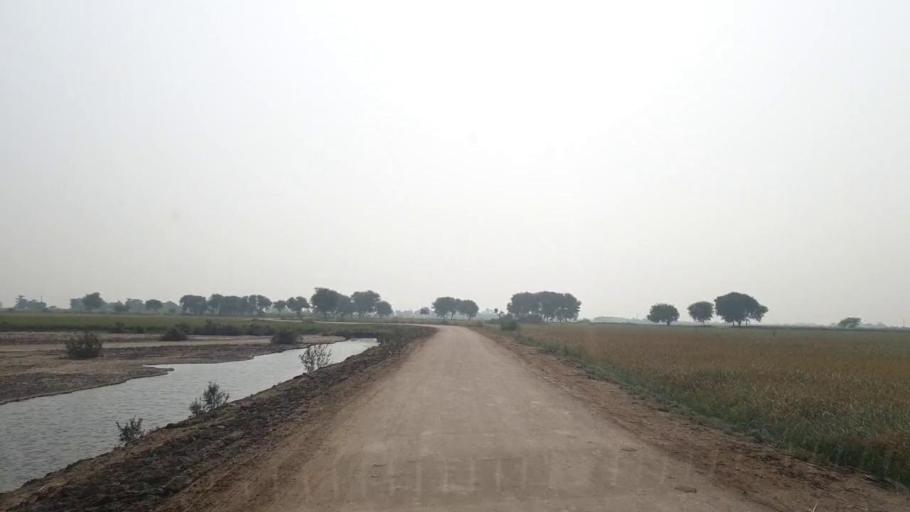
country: PK
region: Sindh
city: Matli
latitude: 25.1310
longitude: 68.7026
